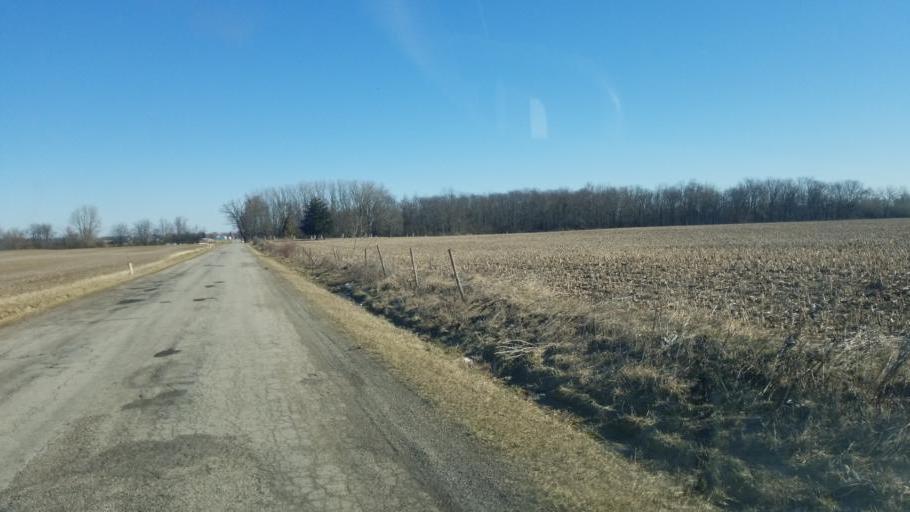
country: US
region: Ohio
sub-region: Morrow County
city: Mount Gilead
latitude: 40.6202
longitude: -82.9184
